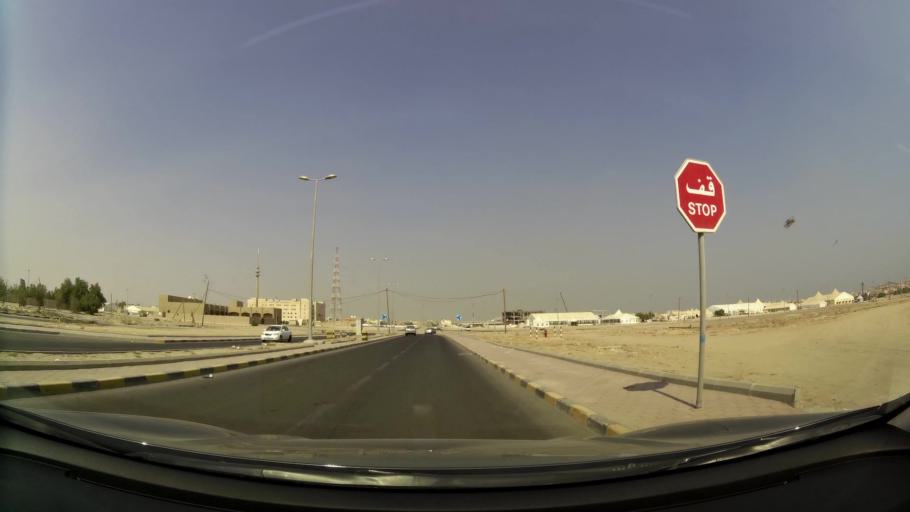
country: KW
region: Al Ahmadi
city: Al Fahahil
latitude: 29.0815
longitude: 48.1078
